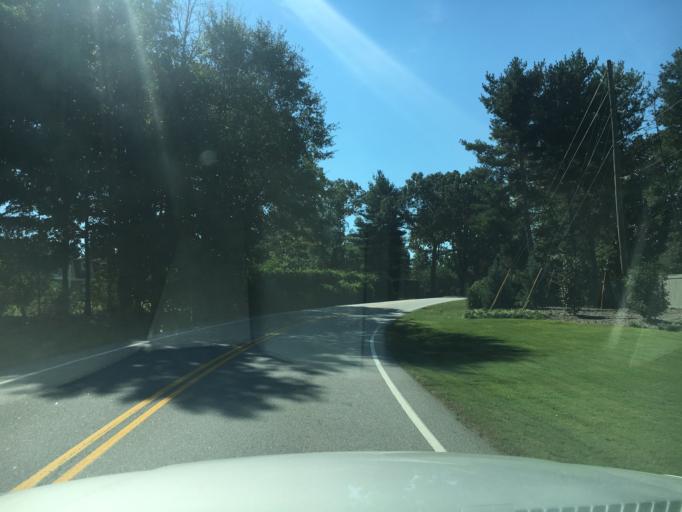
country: US
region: South Carolina
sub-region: Greenville County
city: Taylors
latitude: 34.8746
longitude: -82.2823
